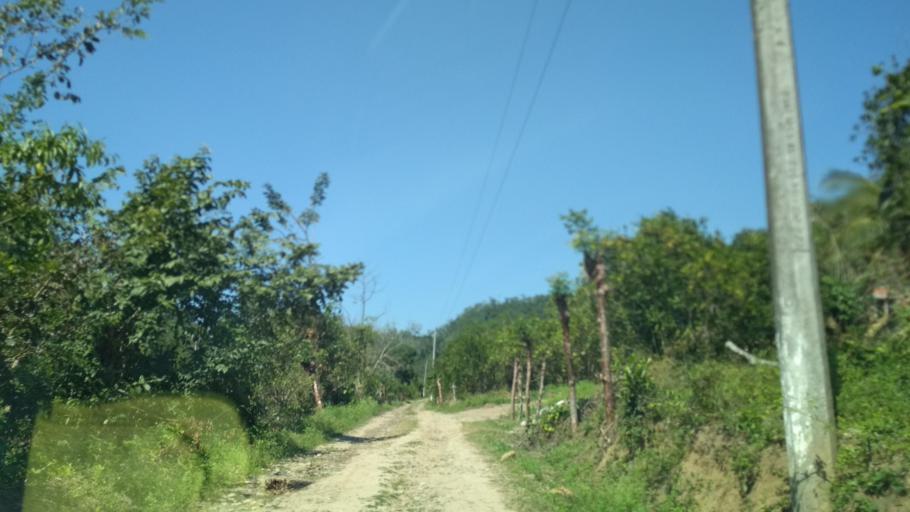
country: MX
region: Veracruz
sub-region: Papantla
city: Polutla
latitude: 20.4849
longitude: -97.2284
